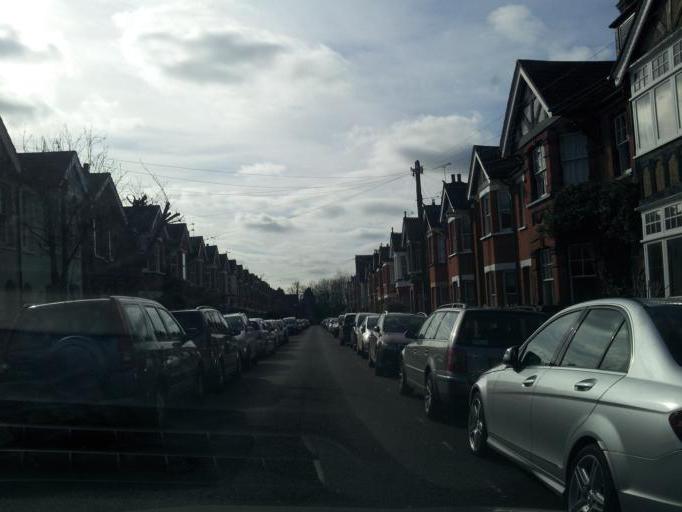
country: GB
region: England
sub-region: Hertfordshire
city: St Albans
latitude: 51.7544
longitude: -0.3189
